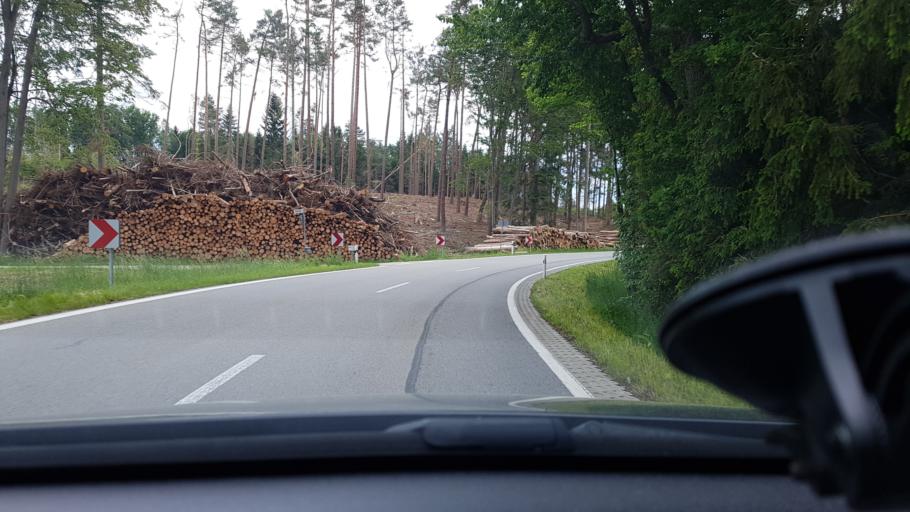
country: DE
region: Bavaria
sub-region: Lower Bavaria
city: Triftern
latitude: 48.3706
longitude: 13.0067
